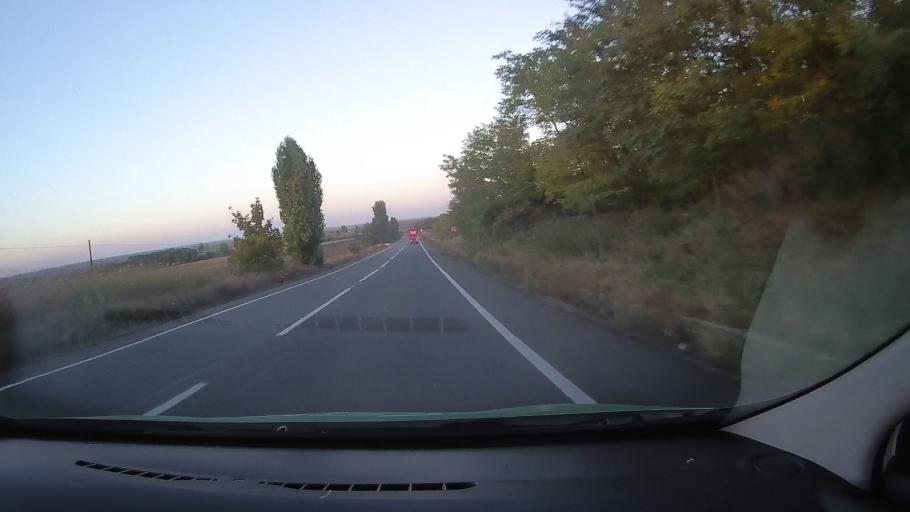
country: RO
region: Bihor
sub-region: Comuna Cherechiu
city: Cherechiu
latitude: 47.3803
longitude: 22.1409
